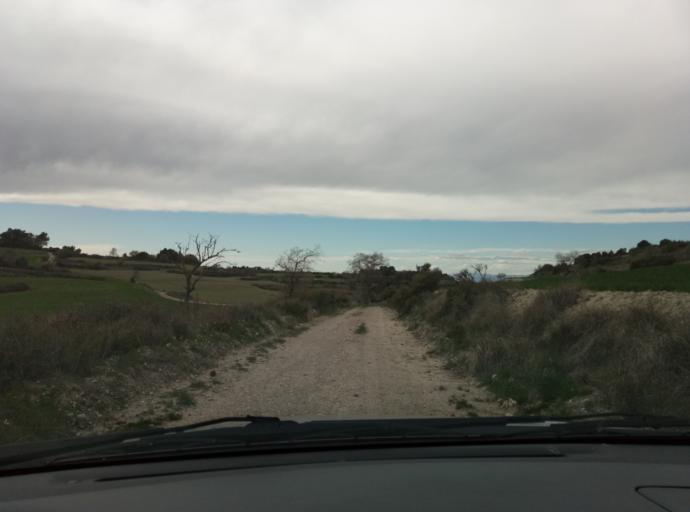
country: ES
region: Catalonia
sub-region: Provincia de Lleida
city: Ciutadilla
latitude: 41.5174
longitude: 1.1624
